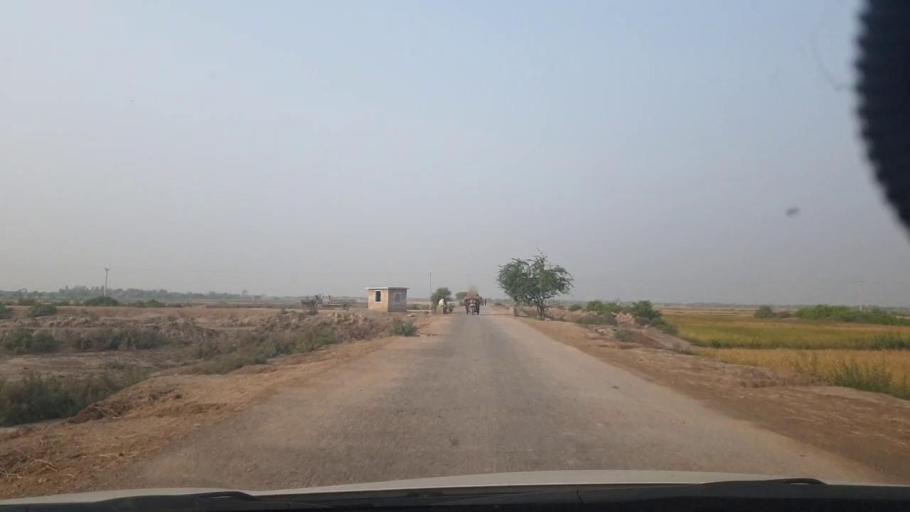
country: PK
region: Sindh
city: Bulri
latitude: 24.7861
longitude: 68.4193
